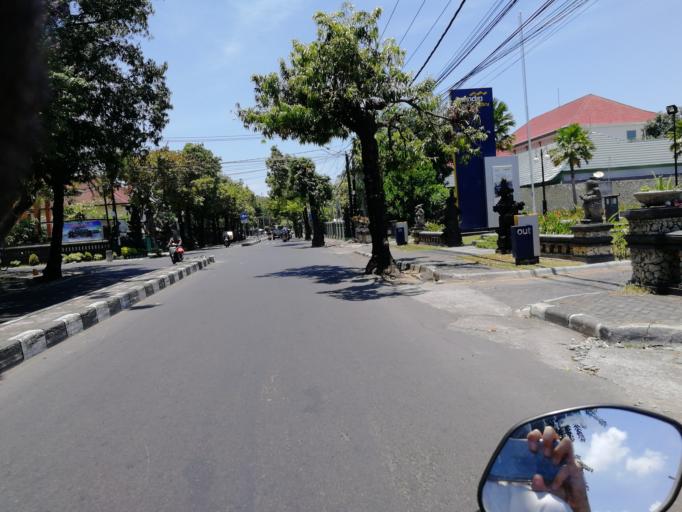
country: ID
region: Bali
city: Denpasar
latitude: -8.6676
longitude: 115.2163
